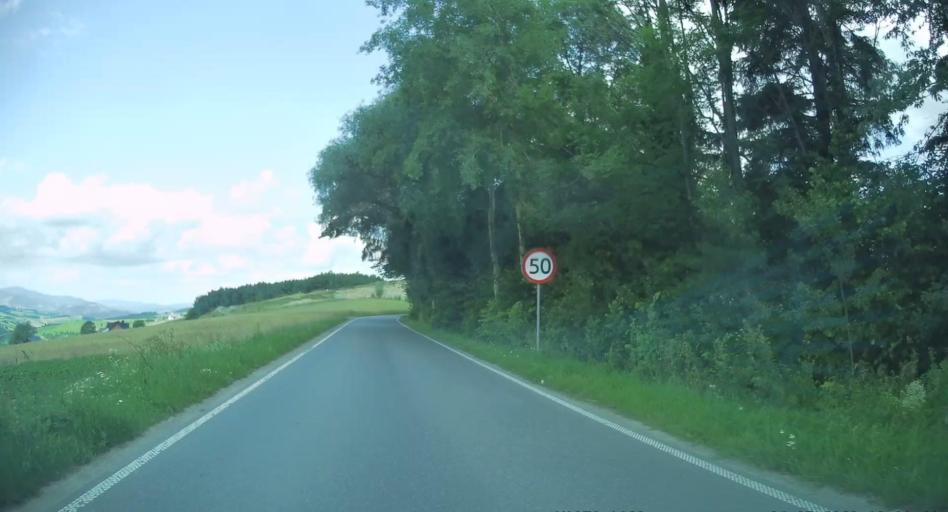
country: PL
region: Lesser Poland Voivodeship
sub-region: Powiat nowosadecki
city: Korzenna
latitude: 49.6988
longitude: 20.7613
